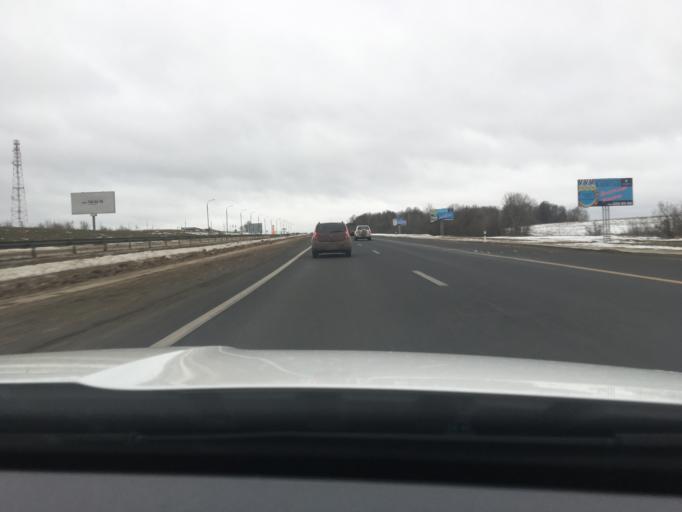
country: RU
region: Moskovskaya
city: Serpukhov
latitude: 54.8504
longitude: 37.4683
